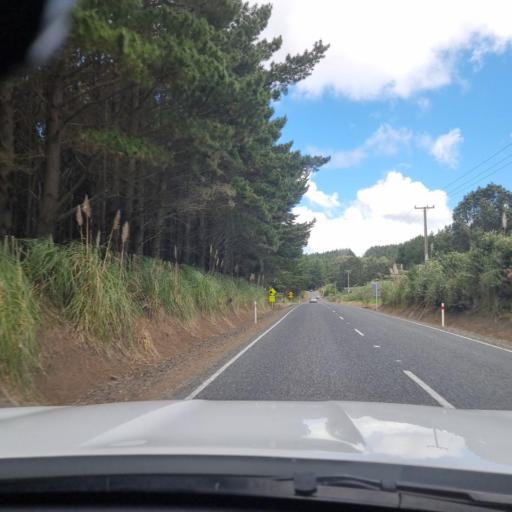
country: NZ
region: Northland
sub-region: Kaipara District
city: Dargaville
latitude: -36.2376
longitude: 174.0468
